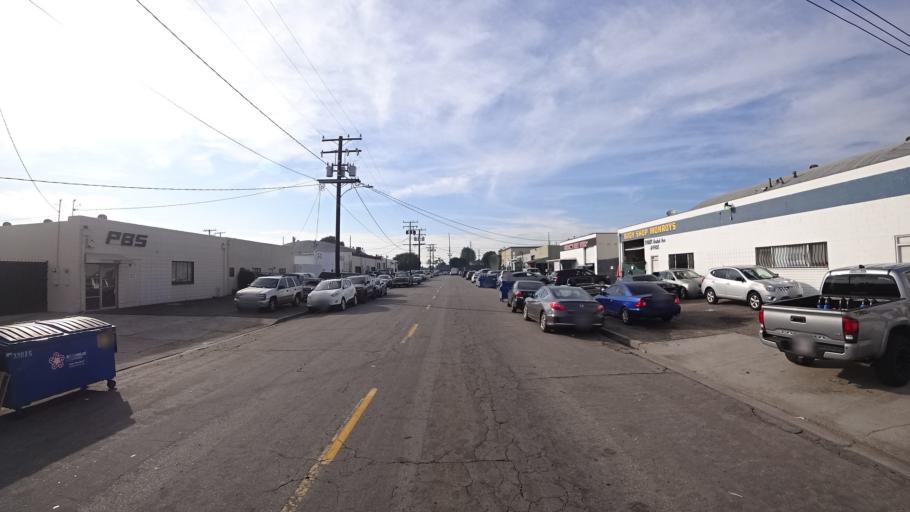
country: US
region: California
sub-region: Orange County
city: Garden Grove
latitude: 33.7629
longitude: -117.9271
